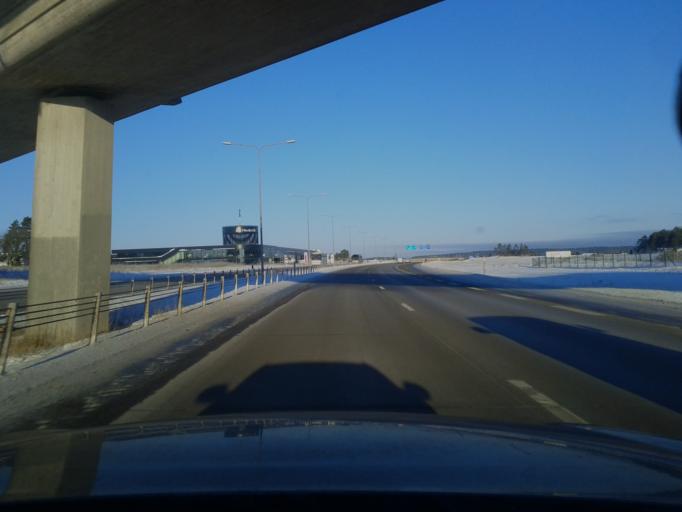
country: SE
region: Uppsala
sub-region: Uppsala Kommun
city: Saevja
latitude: 59.8367
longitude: 17.7324
